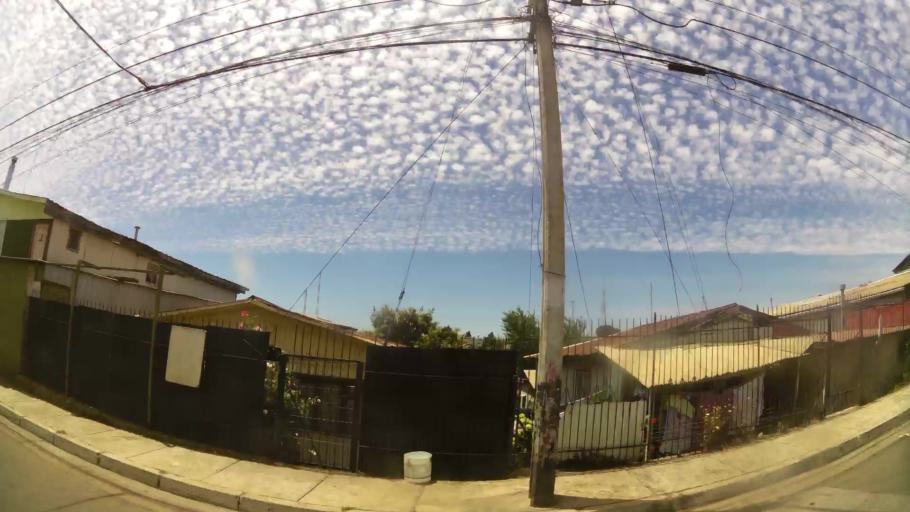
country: CL
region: Valparaiso
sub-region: Provincia de Valparaiso
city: Vina del Mar
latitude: -33.0523
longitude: -71.5650
